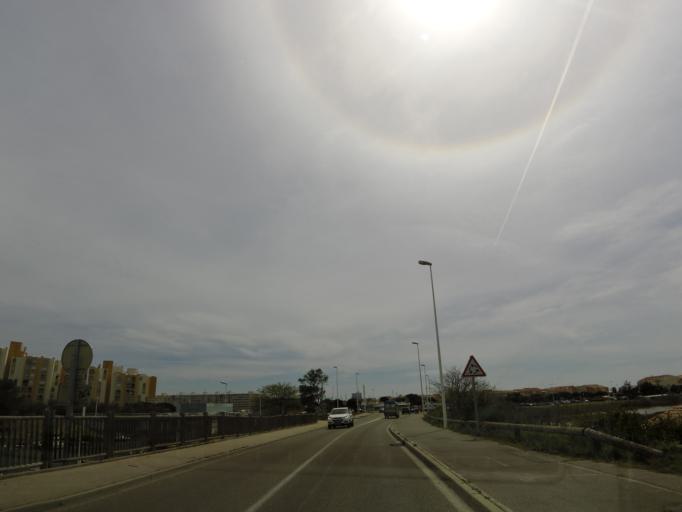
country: FR
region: Languedoc-Roussillon
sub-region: Departement de l'Herault
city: Perols
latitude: 43.5472
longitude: 3.9702
